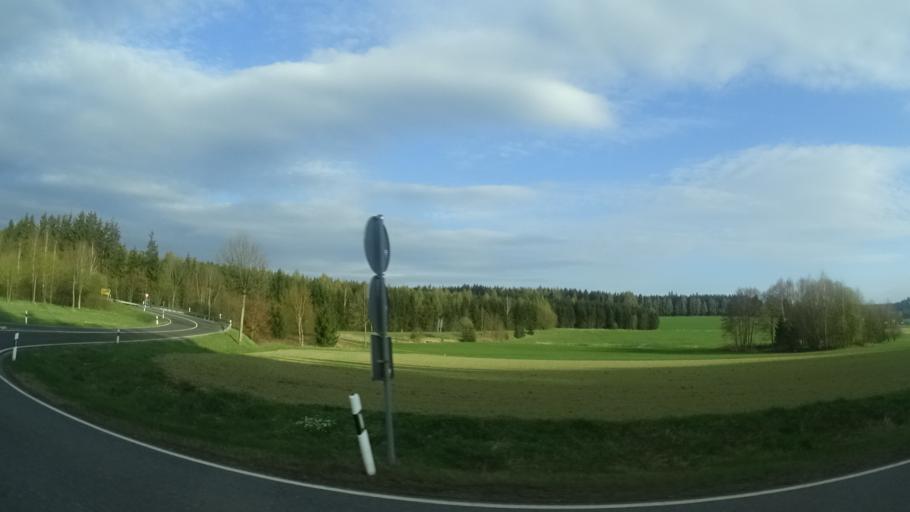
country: DE
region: Bavaria
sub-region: Upper Franconia
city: Leupoldsgrun
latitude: 50.3003
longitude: 11.8270
